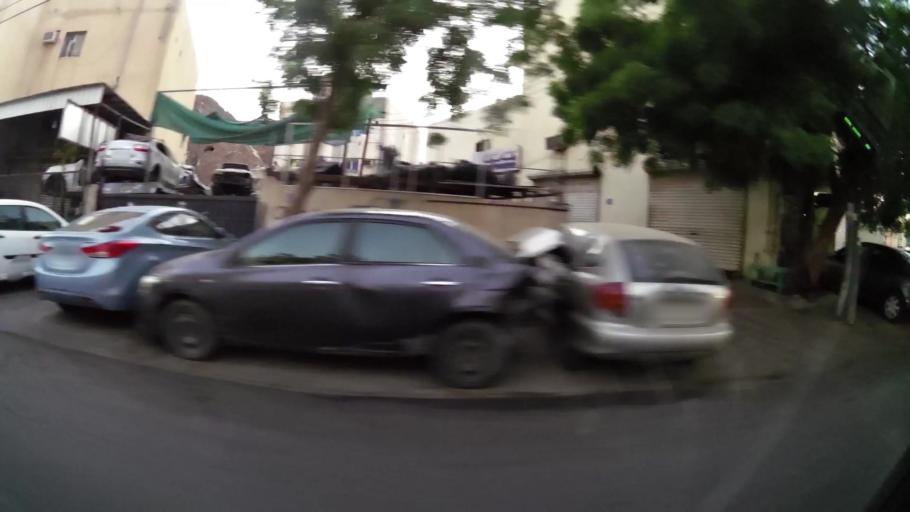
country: OM
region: Muhafazat Masqat
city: Muscat
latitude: 23.5930
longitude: 58.5612
